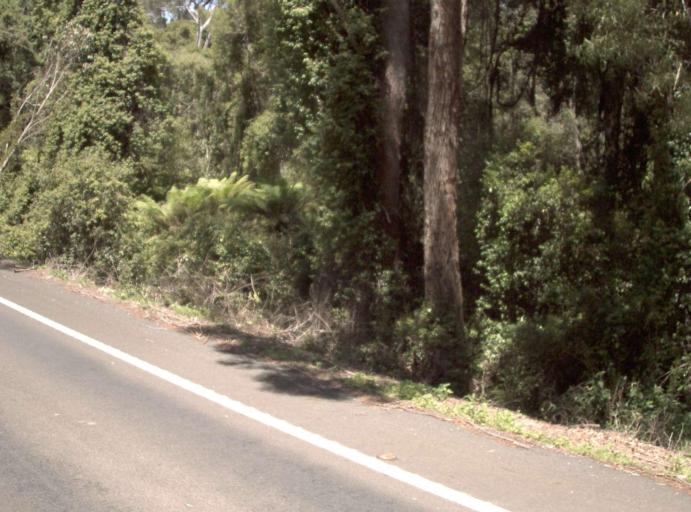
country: AU
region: New South Wales
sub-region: Bombala
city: Bombala
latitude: -37.6080
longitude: 148.8996
